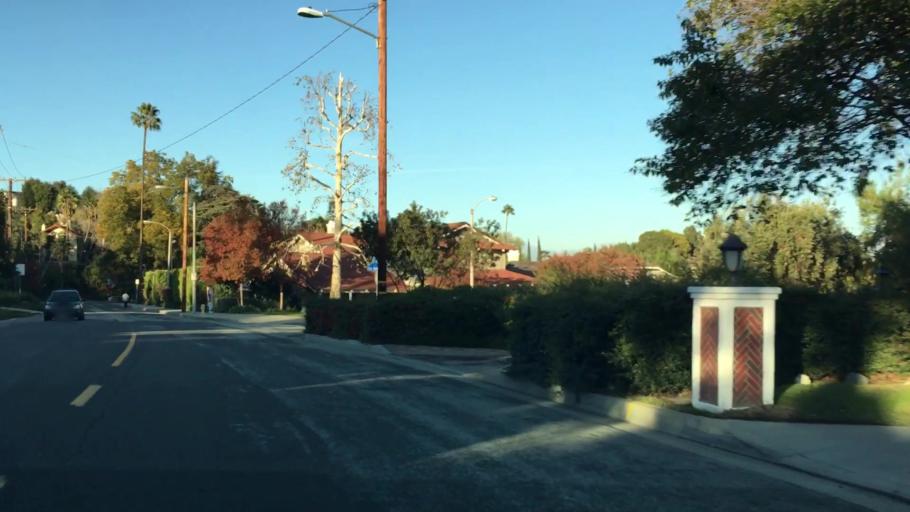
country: US
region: California
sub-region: Los Angeles County
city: Hacienda Heights
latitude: 33.9946
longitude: -117.9871
